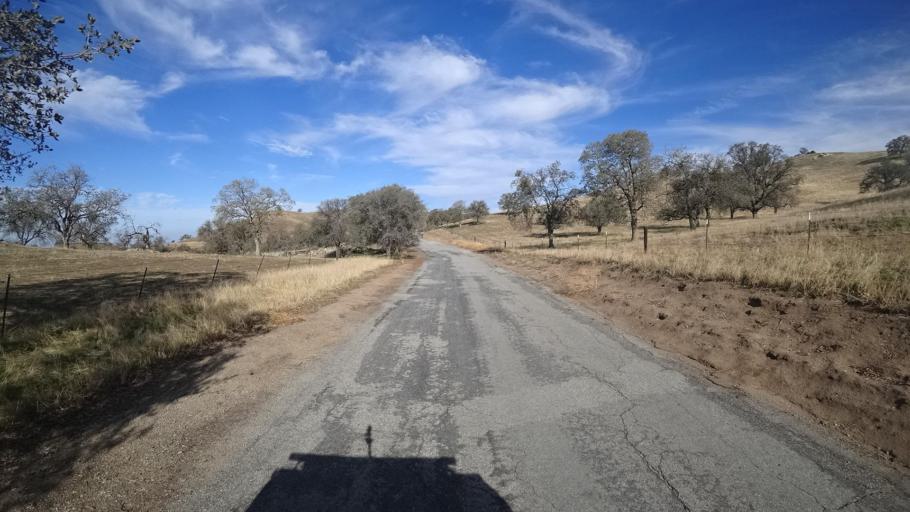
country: US
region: California
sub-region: Kern County
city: Oildale
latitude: 35.6057
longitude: -118.8258
